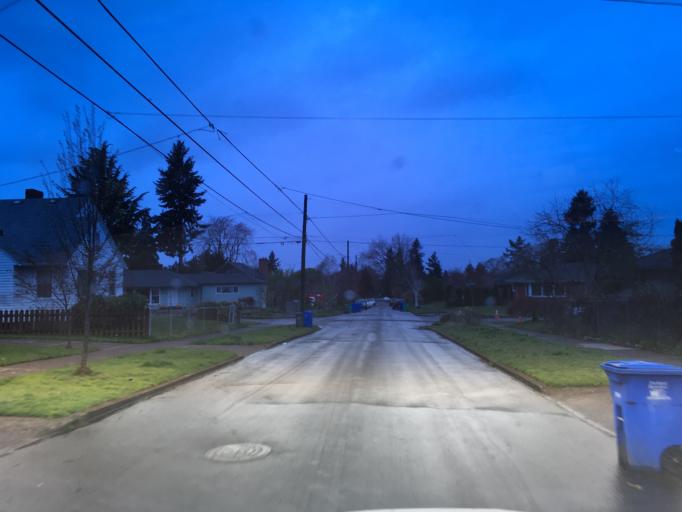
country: US
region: Oregon
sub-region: Multnomah County
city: Lents
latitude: 45.5534
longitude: -122.5973
